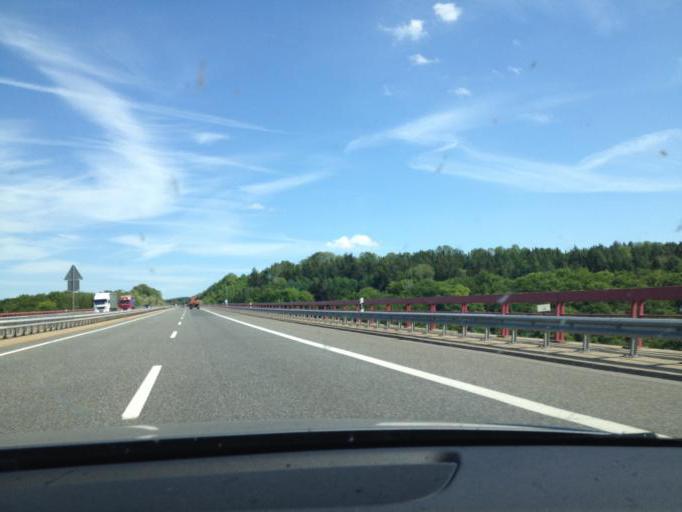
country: DE
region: Rheinland-Pfalz
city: Wilsecker
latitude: 50.0203
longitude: 6.5719
